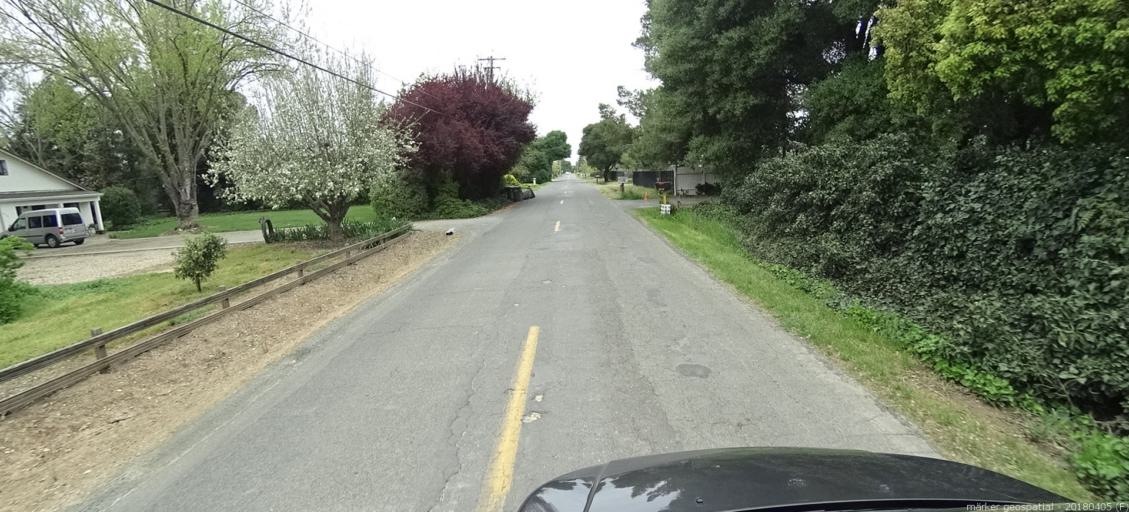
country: US
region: California
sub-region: Sacramento County
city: Galt
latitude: 38.2437
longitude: -121.3261
